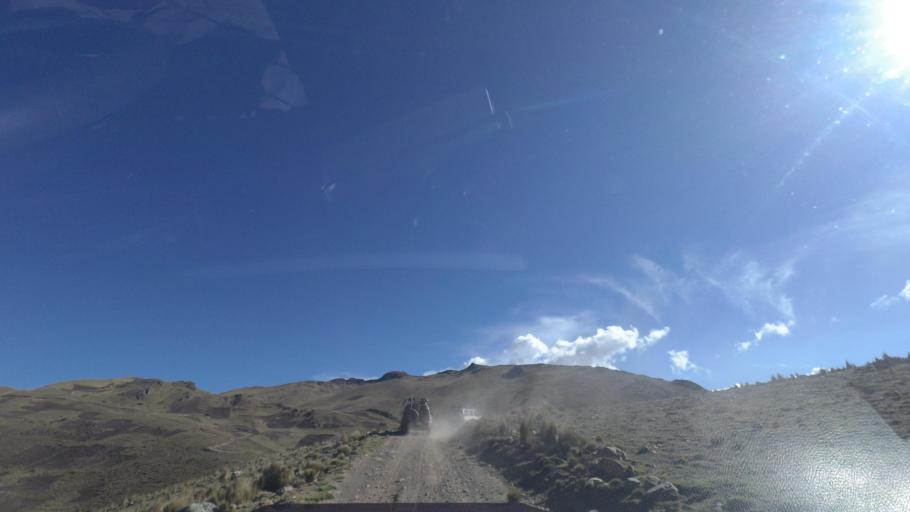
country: BO
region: Cochabamba
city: Cochabamba
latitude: -16.9951
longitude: -66.2709
